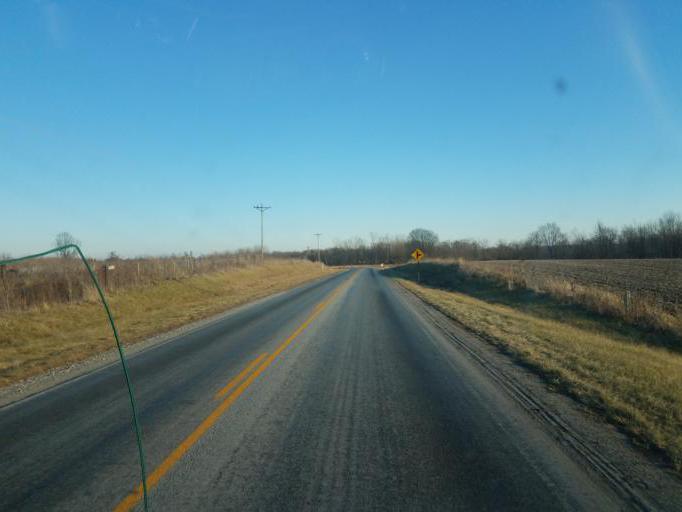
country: US
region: Ohio
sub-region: Hardin County
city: Kenton
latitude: 40.6253
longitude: -83.5323
